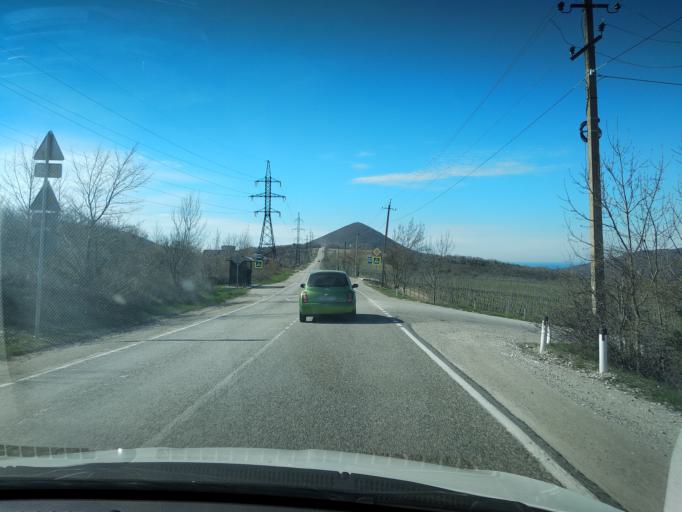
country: RU
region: Krasnodarskiy
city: Myskhako
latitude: 44.6988
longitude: 37.7149
